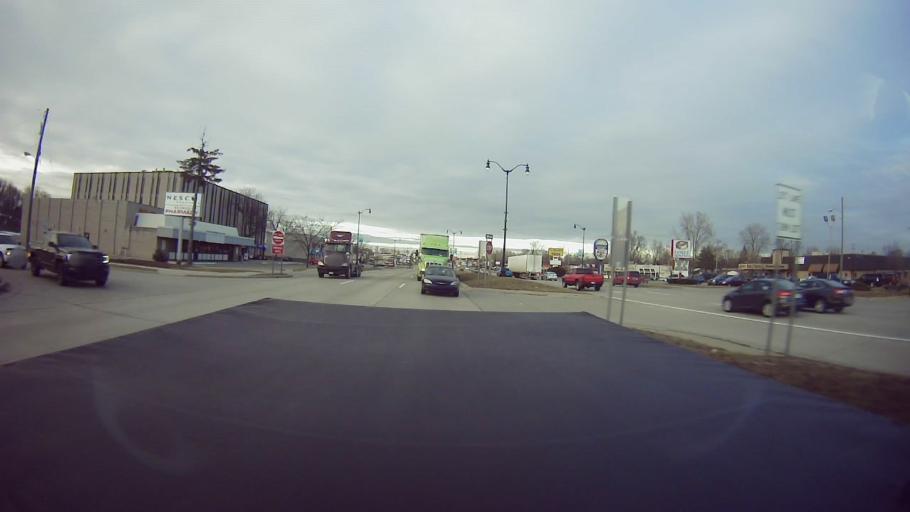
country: US
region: Michigan
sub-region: Wayne County
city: Taylor
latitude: 42.2443
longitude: -83.2699
